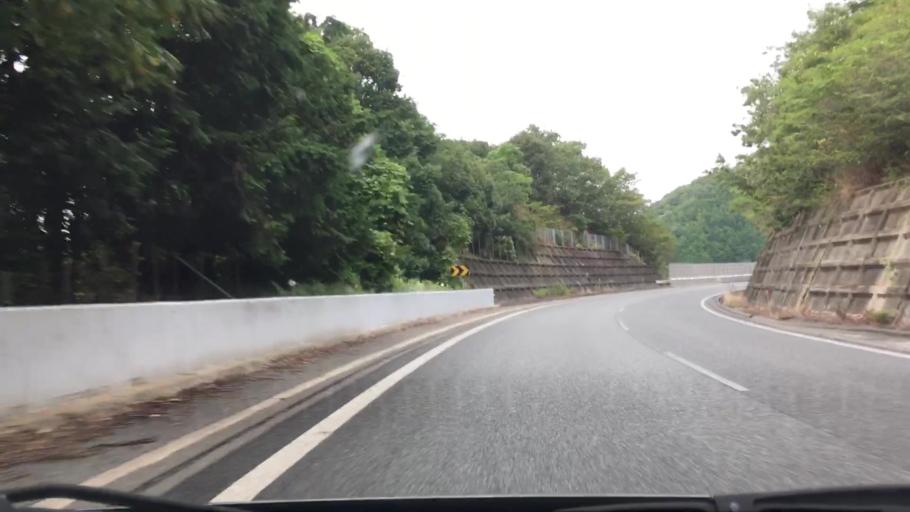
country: JP
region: Okayama
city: Niimi
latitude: 34.9899
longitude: 133.4614
